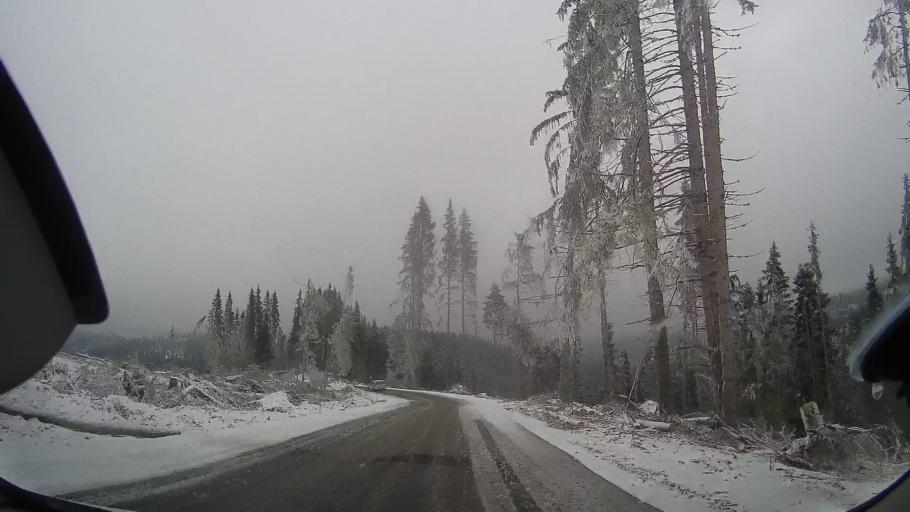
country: RO
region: Cluj
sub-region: Comuna Belis
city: Belis
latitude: 46.6434
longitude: 23.0422
